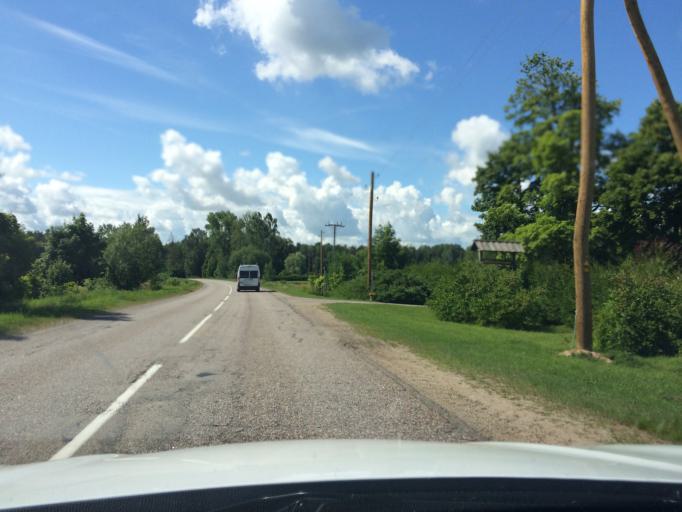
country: LV
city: Tervete
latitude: 56.4964
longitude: 23.4444
